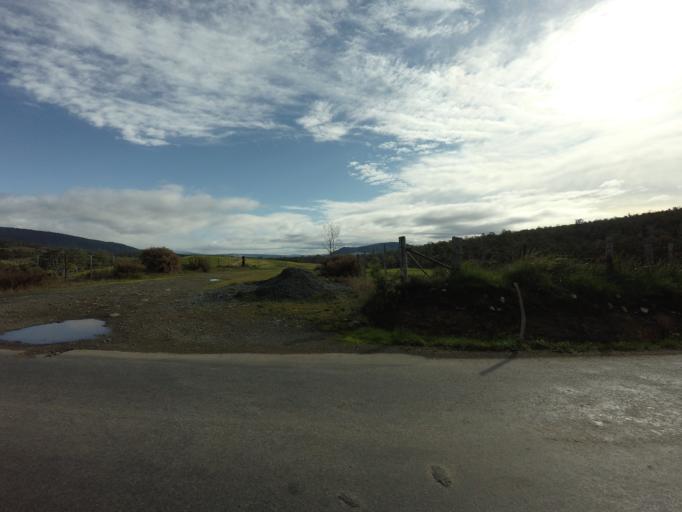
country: AU
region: Tasmania
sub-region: Derwent Valley
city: New Norfolk
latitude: -42.7828
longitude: 146.9988
